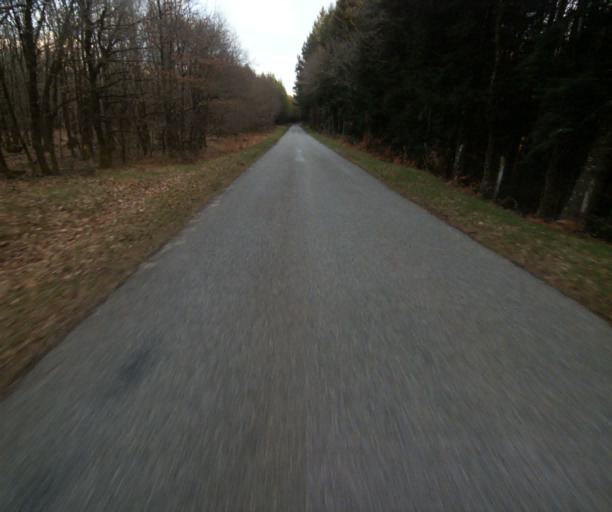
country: FR
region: Limousin
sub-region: Departement de la Correze
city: Correze
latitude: 45.2614
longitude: 1.9775
